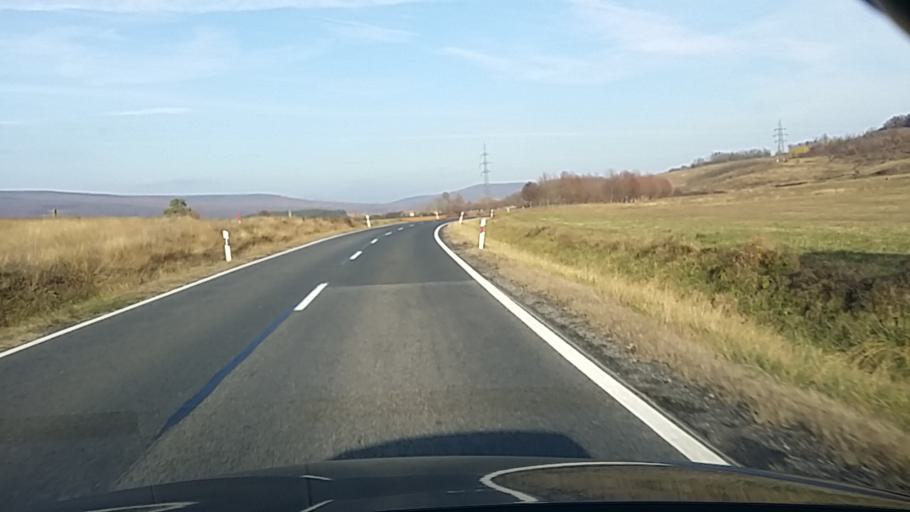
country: HU
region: Veszprem
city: Tapolca
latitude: 46.9018
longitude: 17.5233
